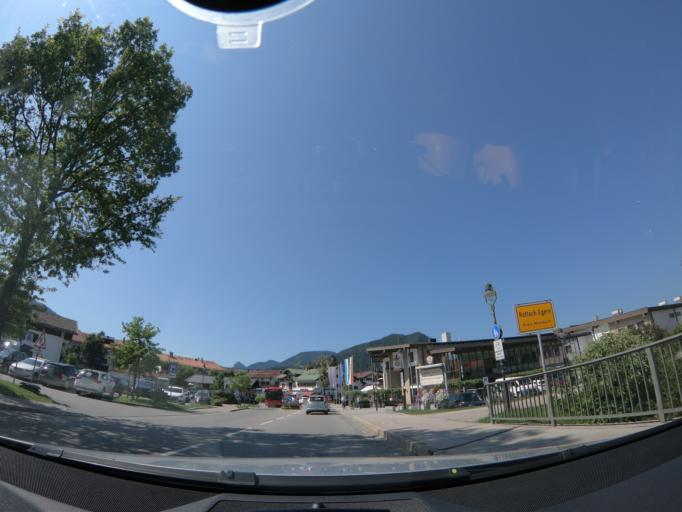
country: DE
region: Bavaria
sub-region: Upper Bavaria
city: Rottach-Egern
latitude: 47.6938
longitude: 11.7714
